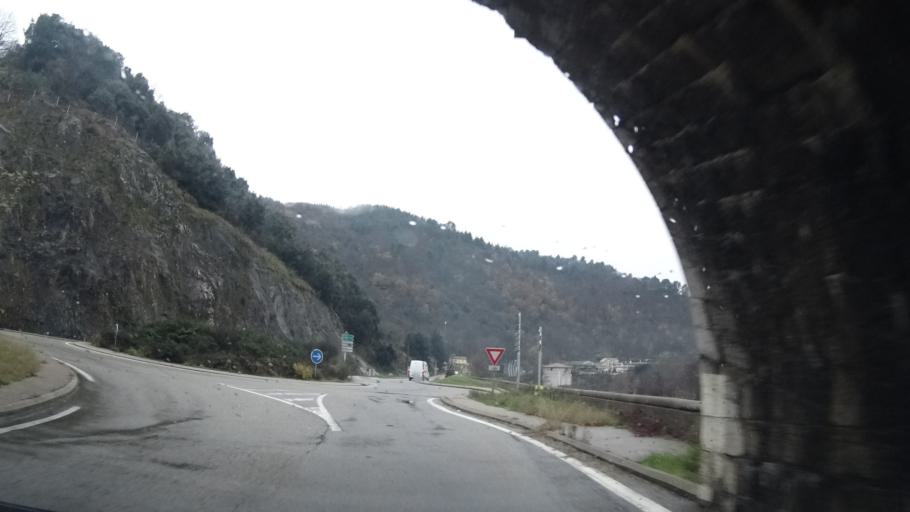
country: FR
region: Rhone-Alpes
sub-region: Departement de l'Ardeche
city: Labegude
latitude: 44.6477
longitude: 4.3553
